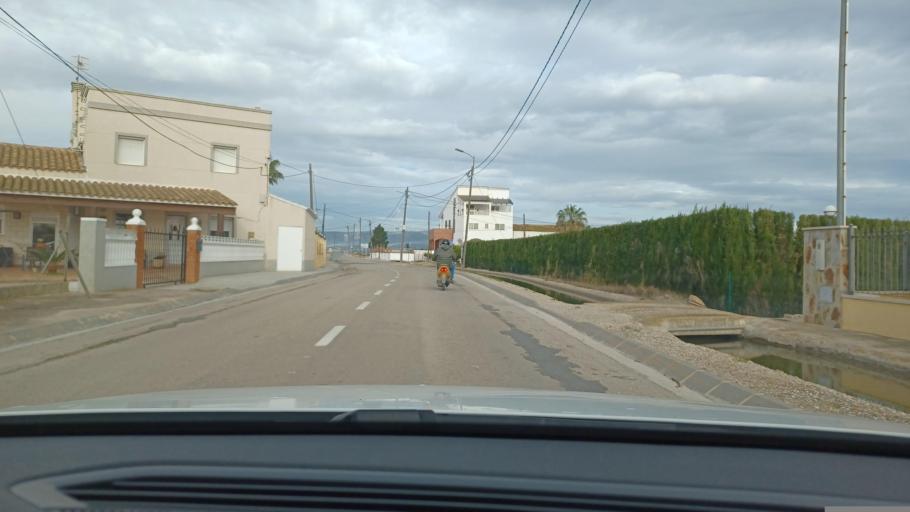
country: ES
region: Catalonia
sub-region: Provincia de Tarragona
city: Deltebre
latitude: 40.7258
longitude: 0.6805
